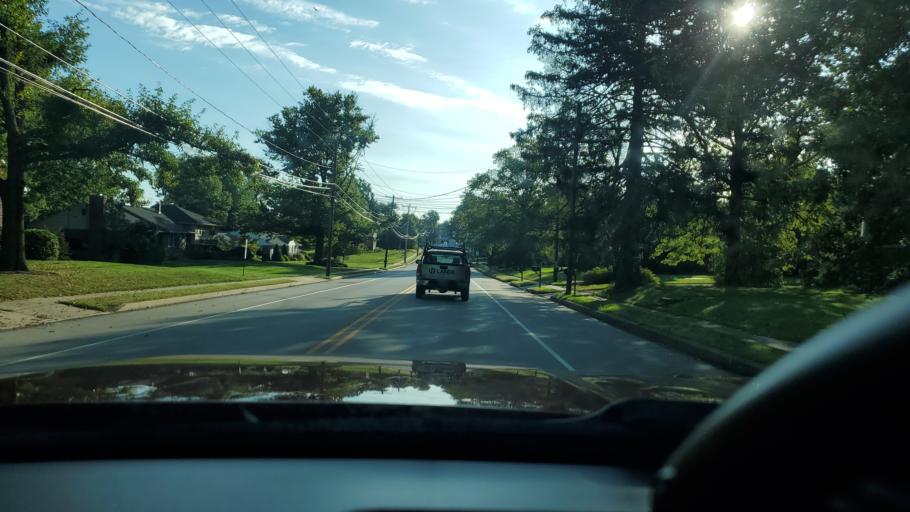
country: US
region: Pennsylvania
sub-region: Montgomery County
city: Telford
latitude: 40.3147
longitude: -75.3387
